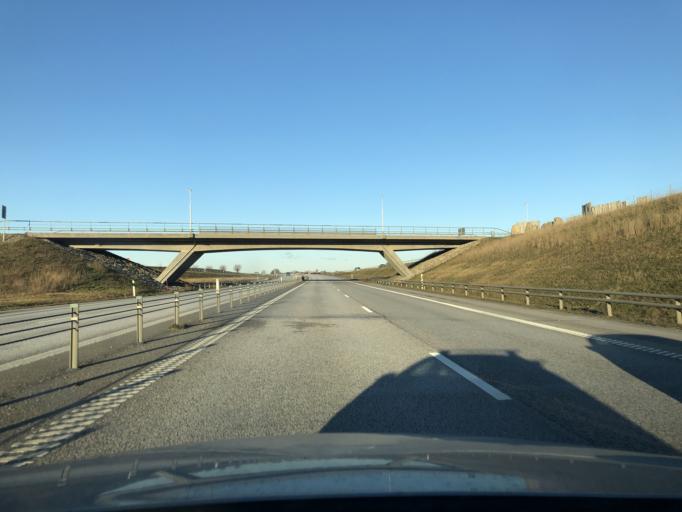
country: SE
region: Skane
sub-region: Trelleborgs Kommun
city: Skare
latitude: 55.4076
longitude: 13.0635
